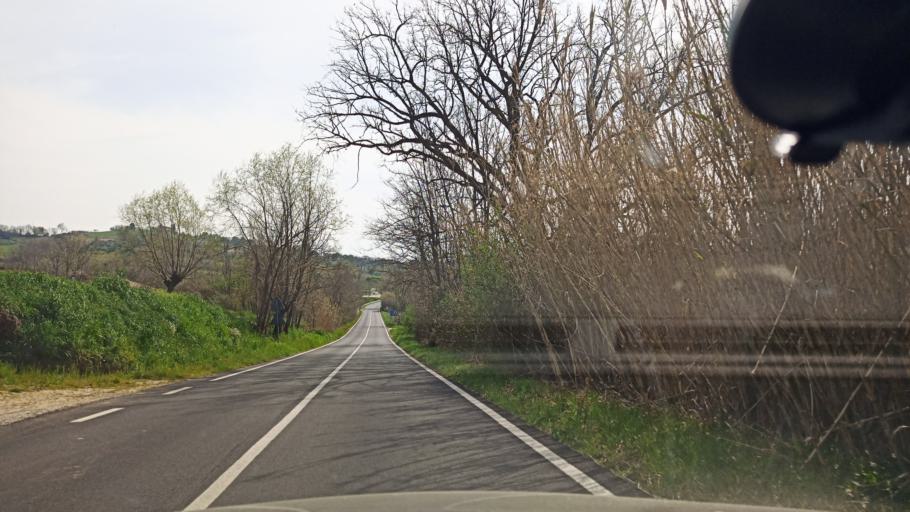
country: IT
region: Latium
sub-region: Provincia di Rieti
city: Cantalupo in Sabina
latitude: 42.3220
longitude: 12.6435
